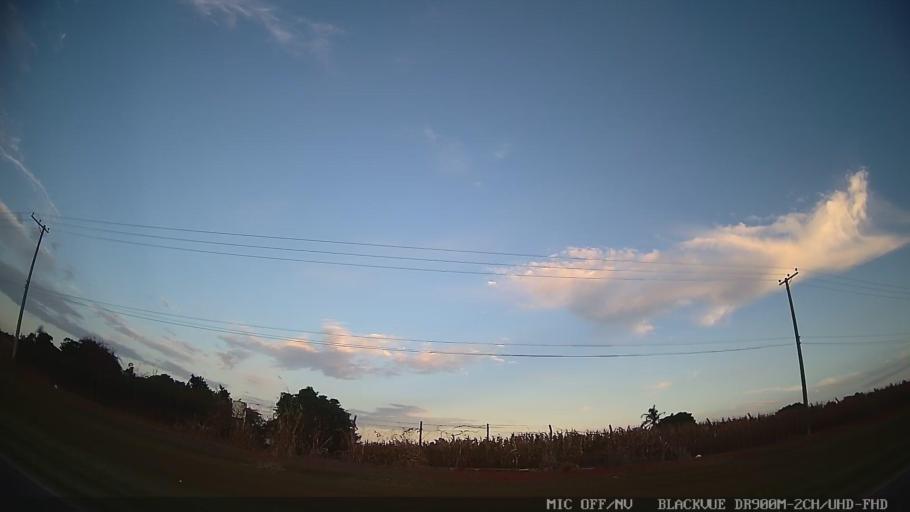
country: BR
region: Sao Paulo
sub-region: Indaiatuba
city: Indaiatuba
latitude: -23.1072
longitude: -47.2043
